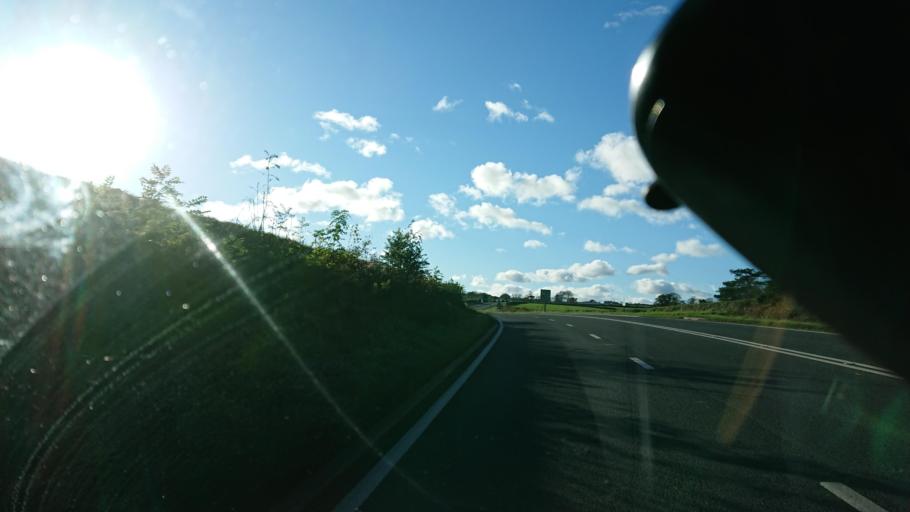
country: GB
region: England
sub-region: Cornwall
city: Pillaton
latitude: 50.4115
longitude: -4.3379
